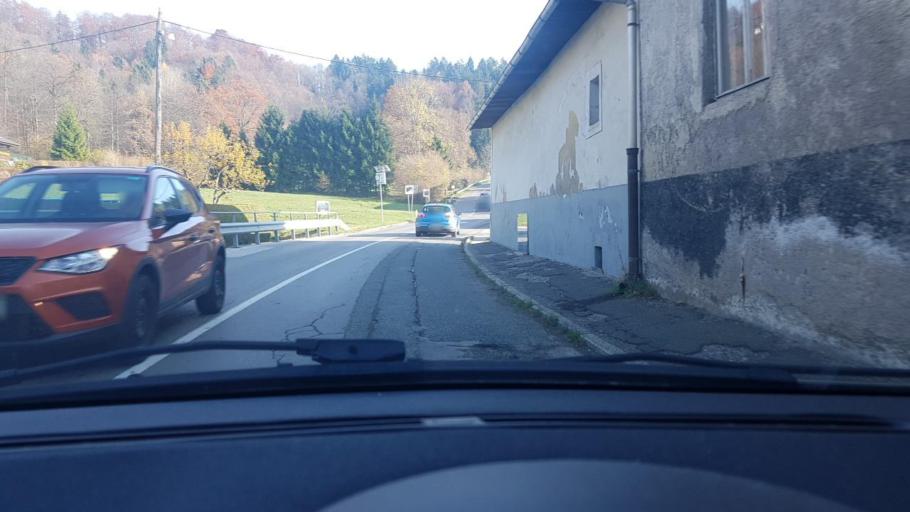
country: SI
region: Trzic
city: Bistrica pri Trzicu
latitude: 46.3380
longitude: 14.3035
